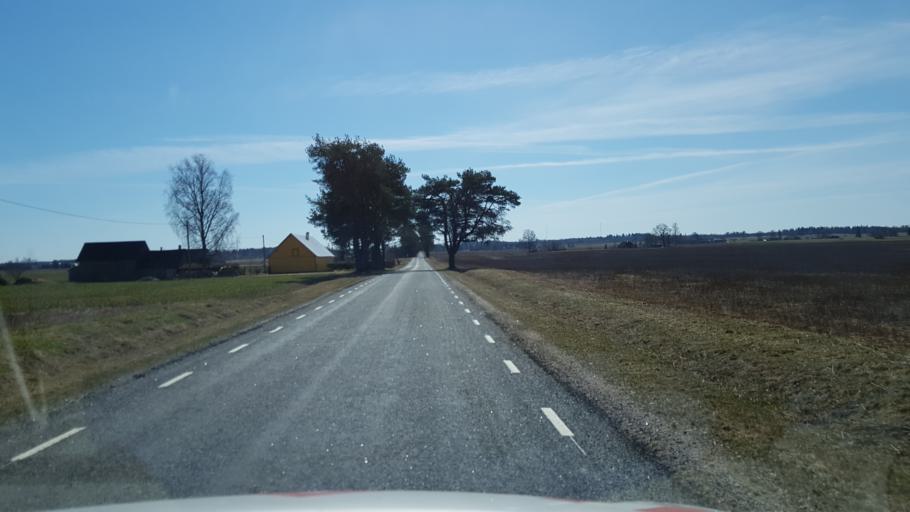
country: EE
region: Laeaene-Virumaa
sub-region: Vinni vald
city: Vinni
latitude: 59.1158
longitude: 26.5235
